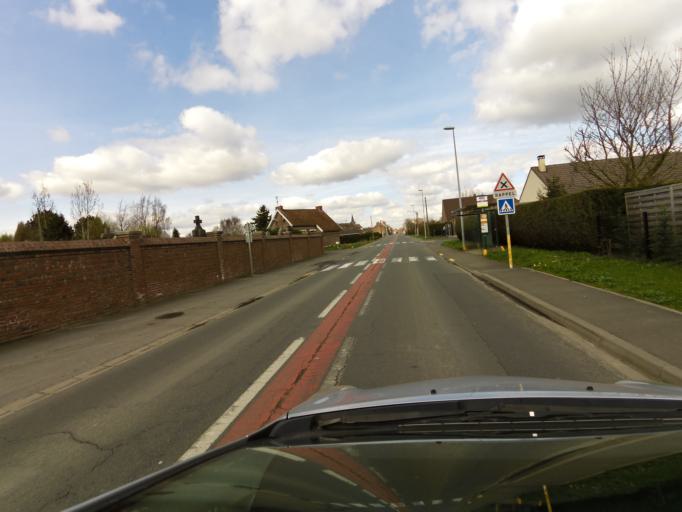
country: FR
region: Nord-Pas-de-Calais
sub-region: Departement du Pas-de-Calais
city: Lorgies
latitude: 50.5802
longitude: 2.7784
